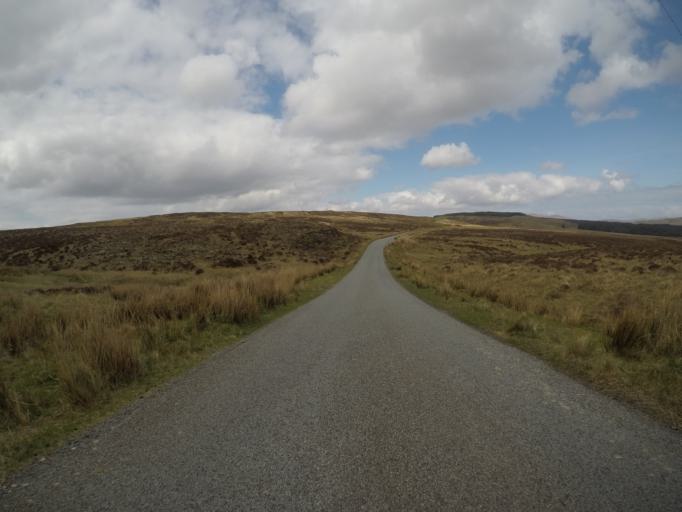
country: GB
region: Scotland
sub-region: Highland
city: Isle of Skye
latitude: 57.4006
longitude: -6.3373
